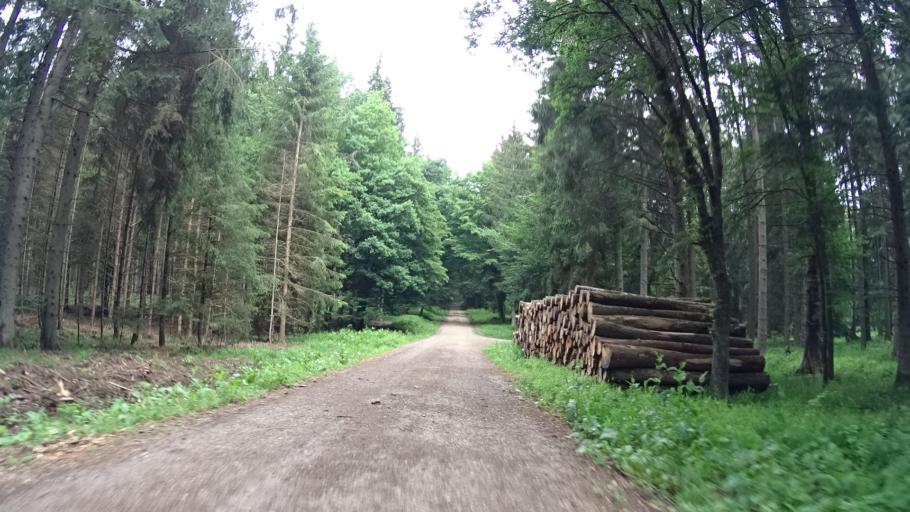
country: DE
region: Bavaria
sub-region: Upper Bavaria
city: Stammham
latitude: 48.8792
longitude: 11.5228
